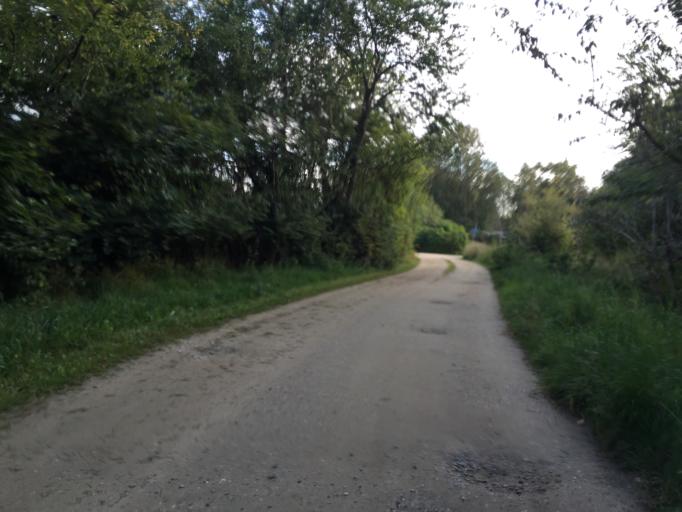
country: DK
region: Zealand
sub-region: Odsherred Kommune
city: Hojby
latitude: 55.9011
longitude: 11.5603
